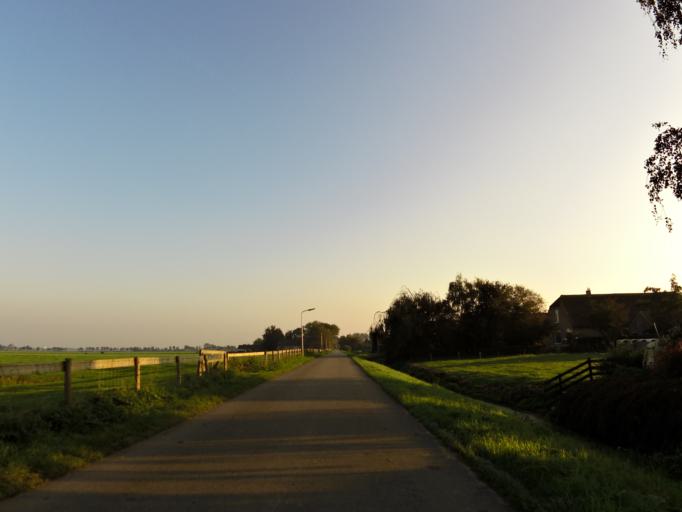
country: NL
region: South Holland
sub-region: Gemeente Leiderdorp
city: Leiderdorp
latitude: 52.1633
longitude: 4.5851
